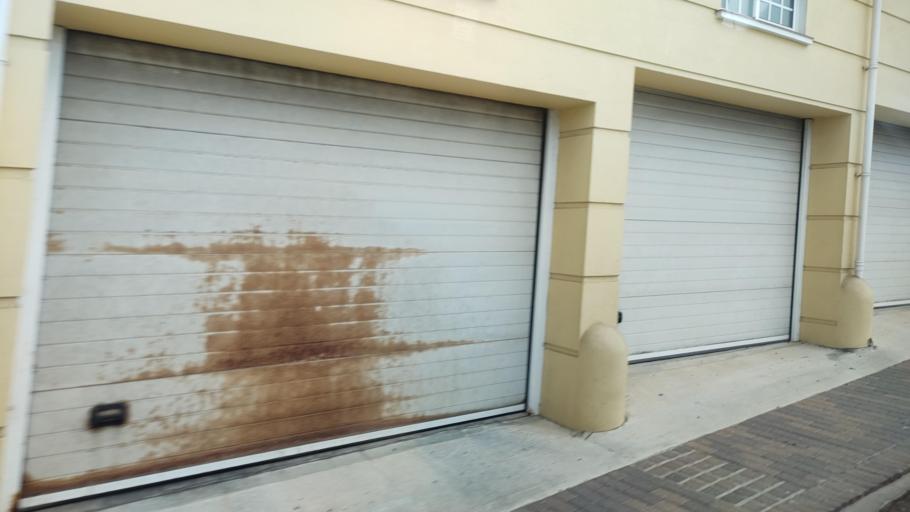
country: GI
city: Gibraltar
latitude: 36.1205
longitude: -5.3472
